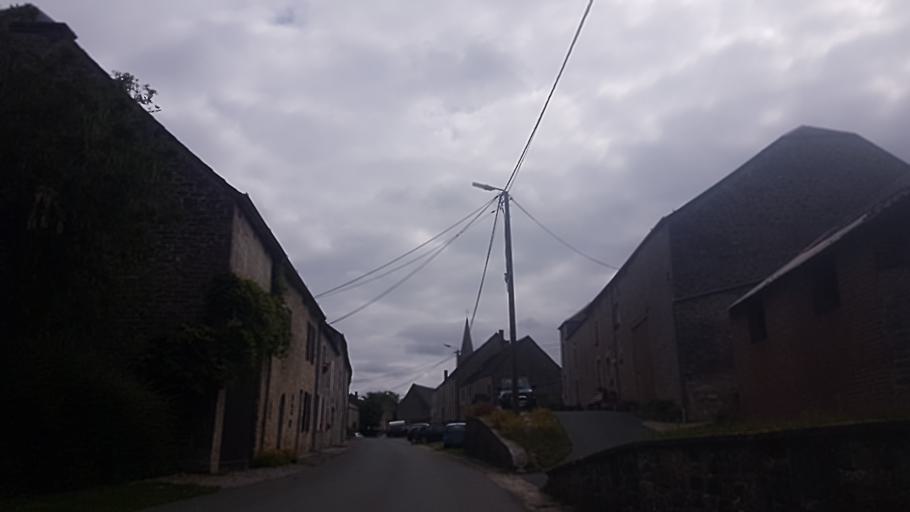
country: BE
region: Wallonia
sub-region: Province de Namur
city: Couvin
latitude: 50.1046
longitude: 4.5681
